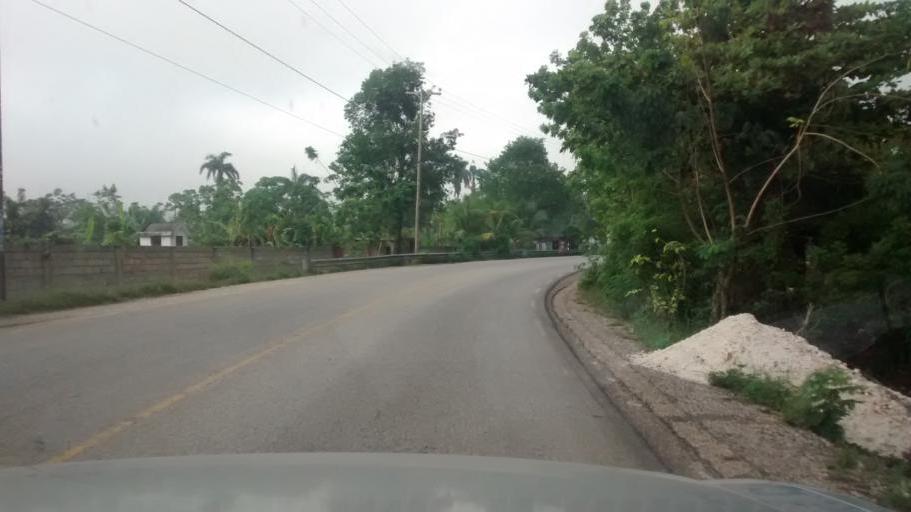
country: HT
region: Sud
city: Fond des Blancs
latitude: 18.3504
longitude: -73.1563
